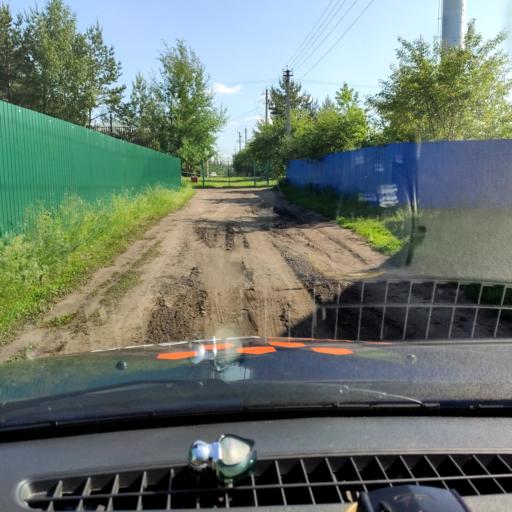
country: RU
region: Voronezj
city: Ramon'
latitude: 51.8936
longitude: 39.2032
